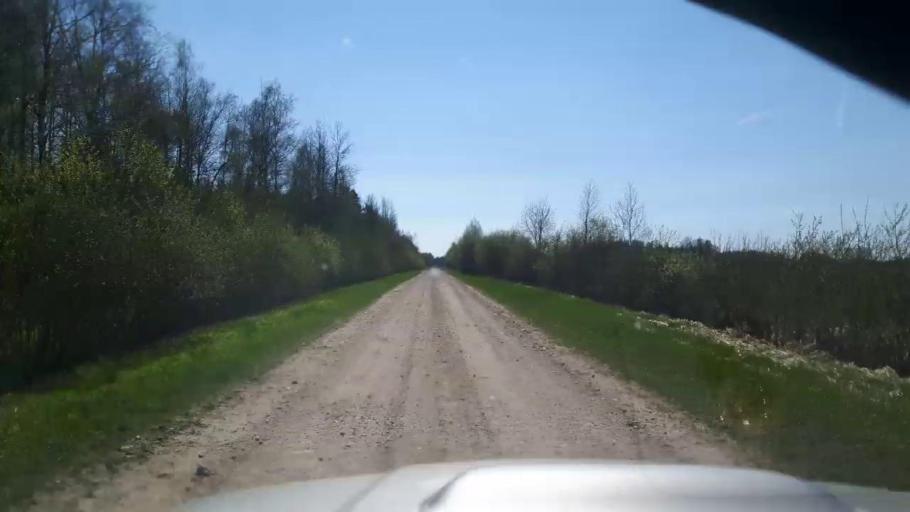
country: EE
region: Paernumaa
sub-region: Tootsi vald
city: Tootsi
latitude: 58.4682
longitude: 24.8129
